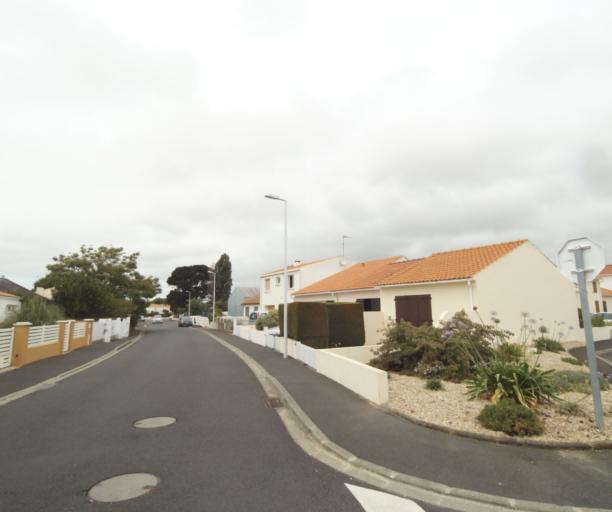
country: FR
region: Pays de la Loire
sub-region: Departement de la Vendee
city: Chateau-d'Olonne
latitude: 46.4889
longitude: -1.7564
